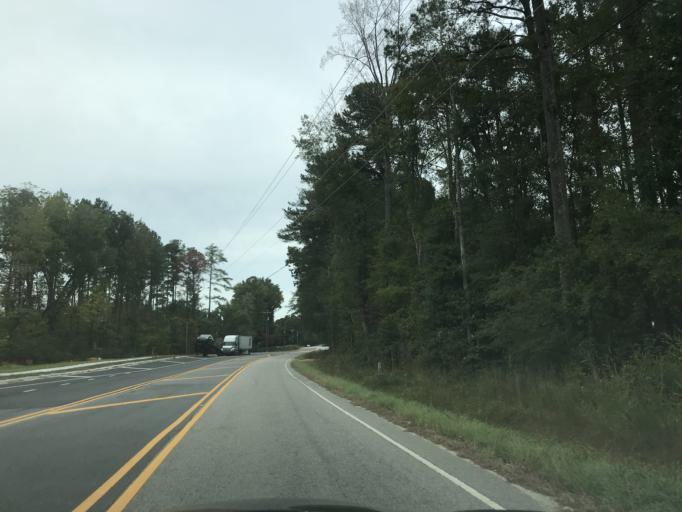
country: US
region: North Carolina
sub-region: Wake County
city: Knightdale
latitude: 35.8361
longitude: -78.5164
